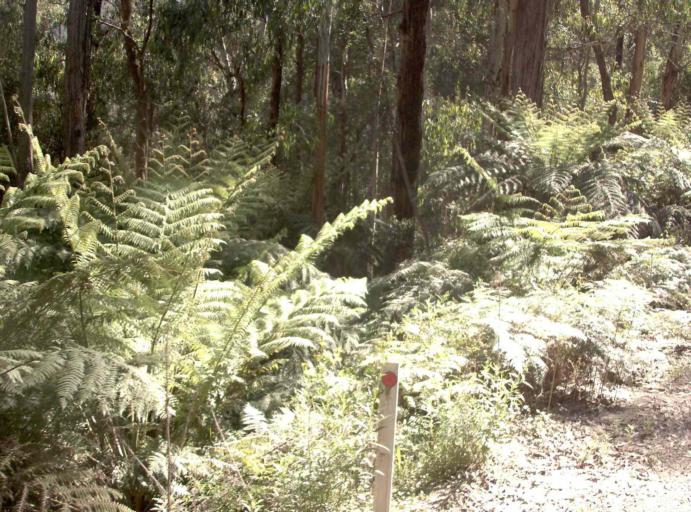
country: AU
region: New South Wales
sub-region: Bombala
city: Bombala
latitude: -37.2502
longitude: 148.7441
